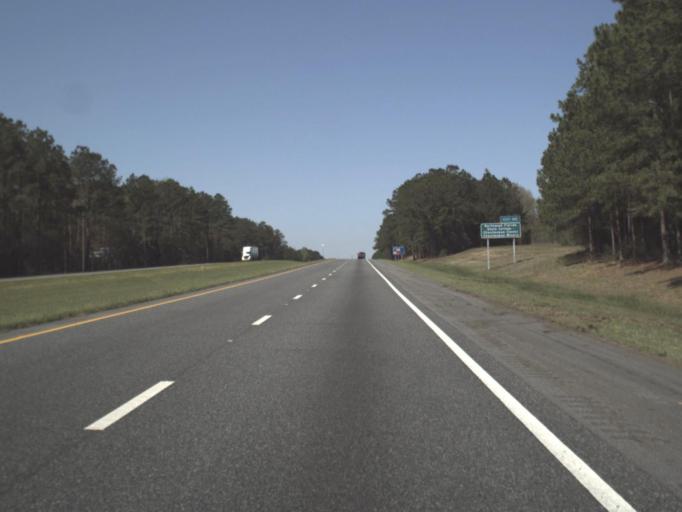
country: US
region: Florida
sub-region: Walton County
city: DeFuniak Springs
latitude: 30.6916
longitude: -86.1031
